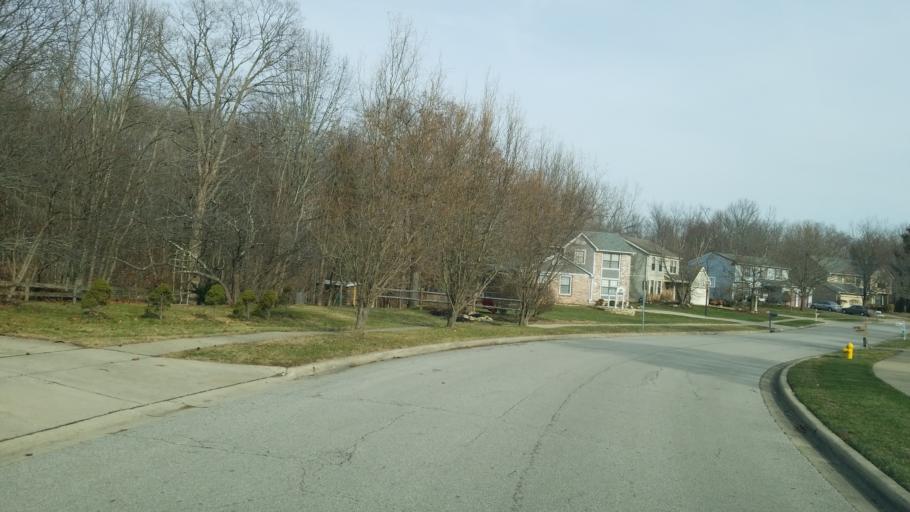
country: US
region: Ohio
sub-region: Delaware County
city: Powell
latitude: 40.1623
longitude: -83.0345
